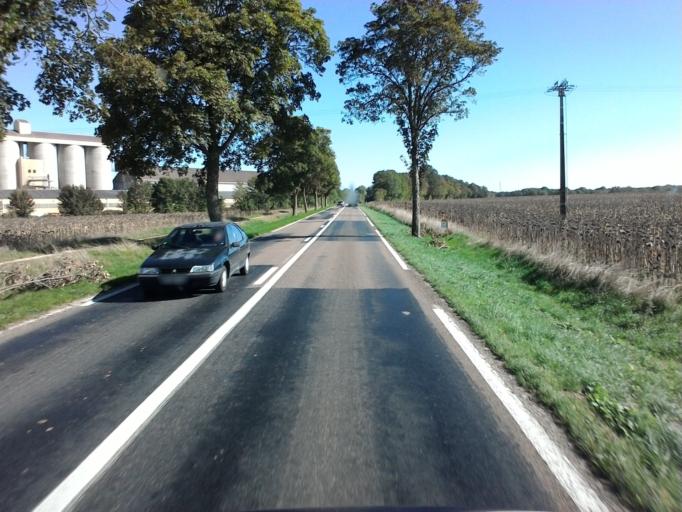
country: FR
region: Champagne-Ardenne
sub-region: Departement de la Haute-Marne
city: Chaumont
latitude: 48.1109
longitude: 5.0861
